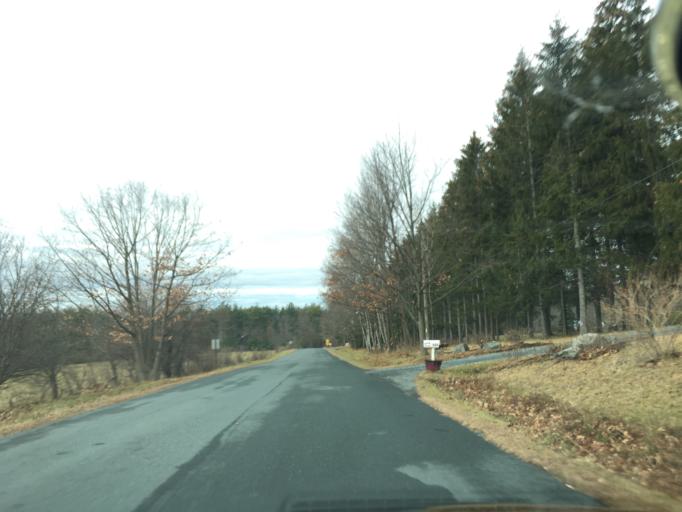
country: US
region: New York
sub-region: Rensselaer County
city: Averill Park
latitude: 42.6109
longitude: -73.5465
